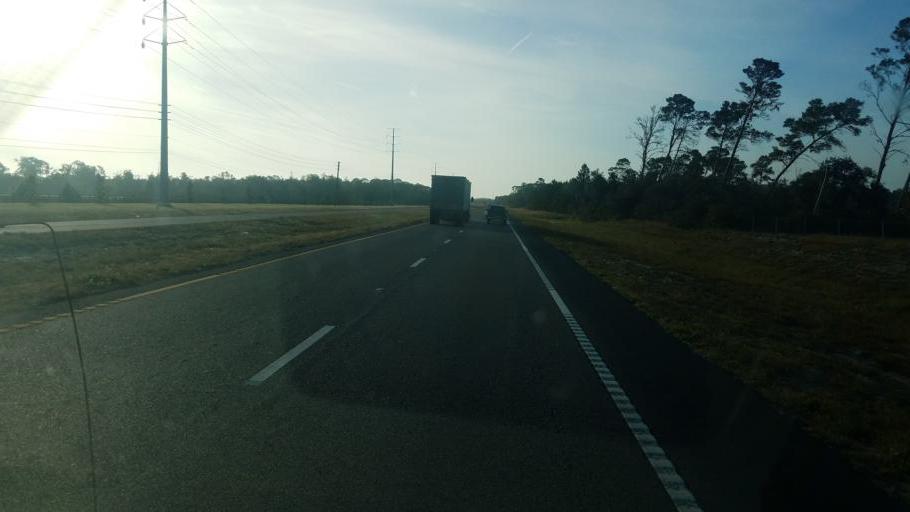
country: US
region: Florida
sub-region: Osceola County
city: Saint Cloud
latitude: 28.2091
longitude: -81.1726
